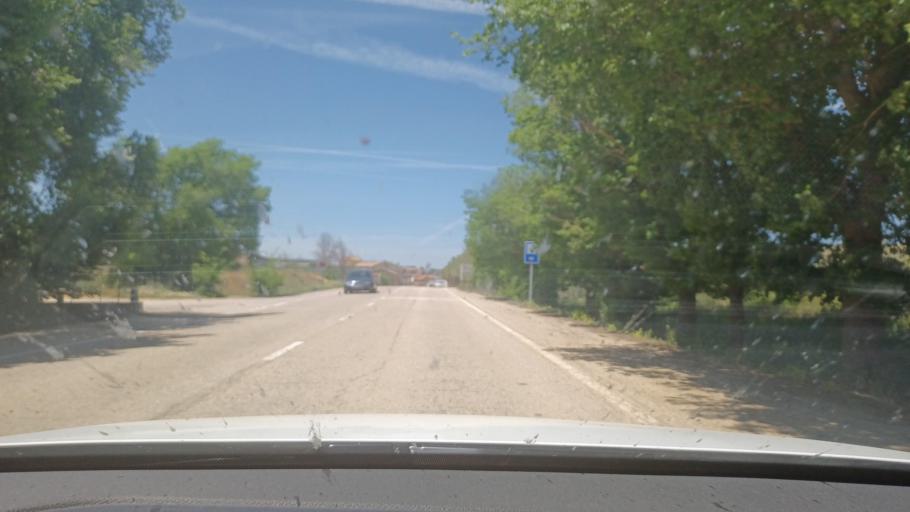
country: ES
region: Castille-La Mancha
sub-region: Provincia de Cuenca
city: Villares del Saz
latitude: 39.8374
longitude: -2.4996
